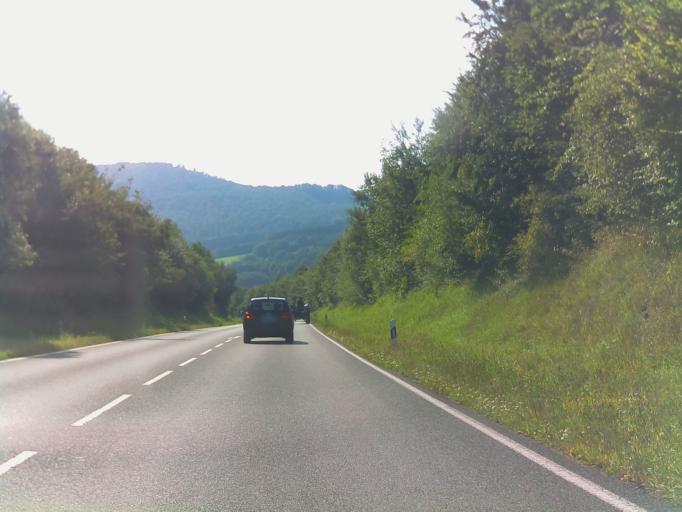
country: DE
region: Bavaria
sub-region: Regierungsbezirk Unterfranken
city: Wildflecken
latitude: 50.3729
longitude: 9.9083
